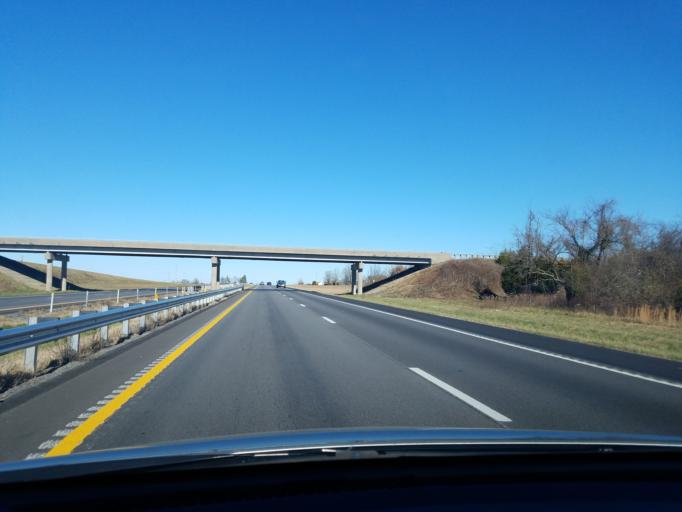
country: US
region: Missouri
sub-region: Webster County
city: Marshfield
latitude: 37.3824
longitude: -92.9028
